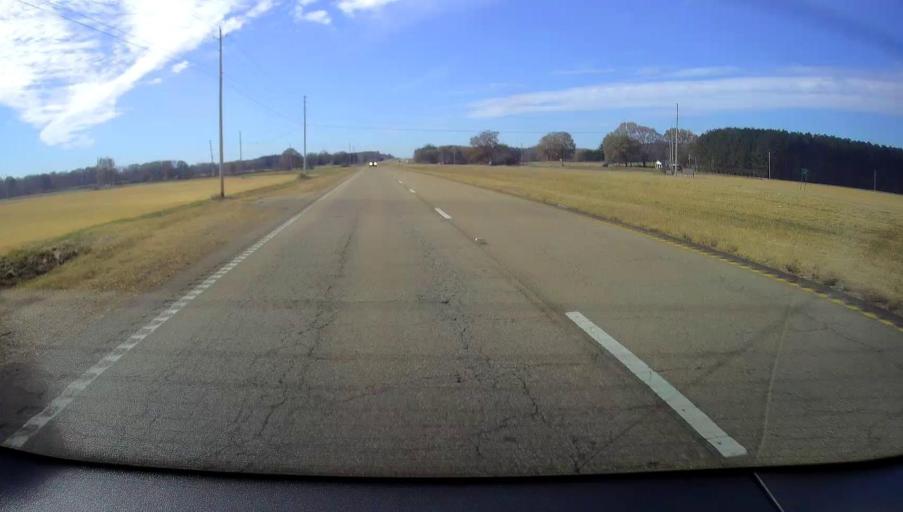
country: US
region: Mississippi
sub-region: Alcorn County
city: Corinth
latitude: 34.9317
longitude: -88.6619
